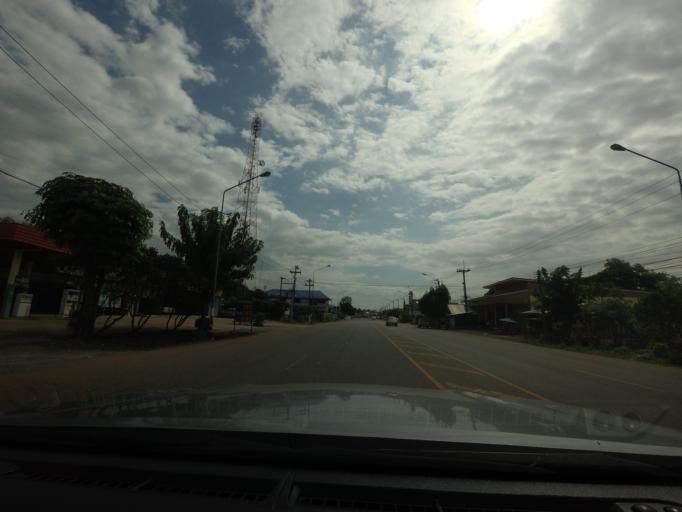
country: TH
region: Phitsanulok
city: Noen Maprang
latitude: 16.5708
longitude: 100.6338
